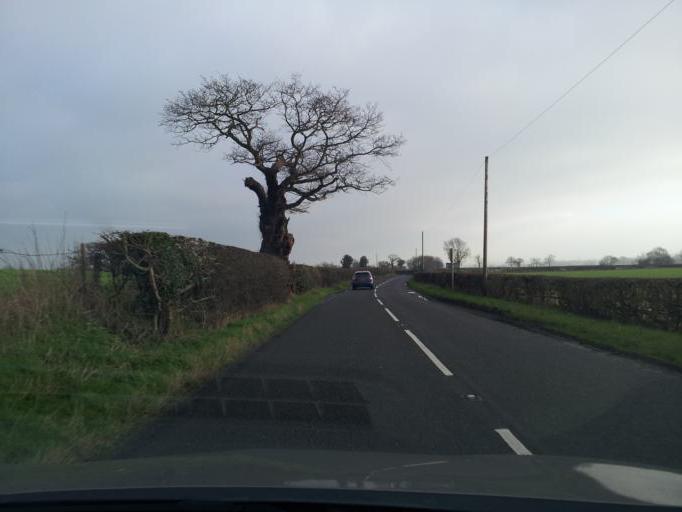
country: GB
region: England
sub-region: Derbyshire
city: Rodsley
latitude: 52.8812
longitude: -1.7521
